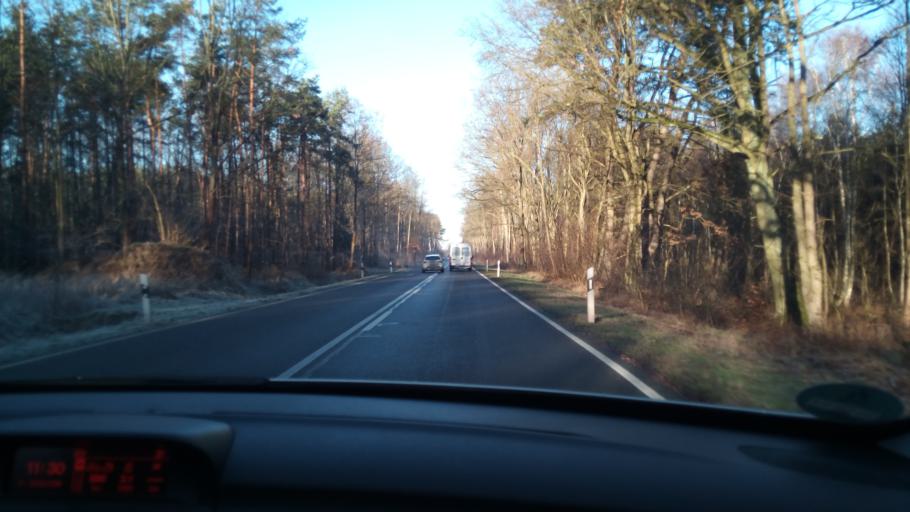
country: DE
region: Mecklenburg-Vorpommern
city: Rechlin
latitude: 53.2992
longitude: 12.7797
